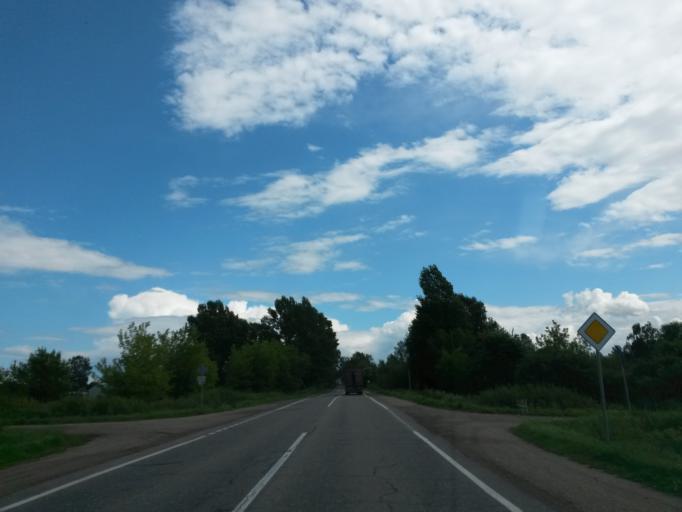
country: RU
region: Jaroslavl
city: Dubki
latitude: 57.2351
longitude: 40.1938
